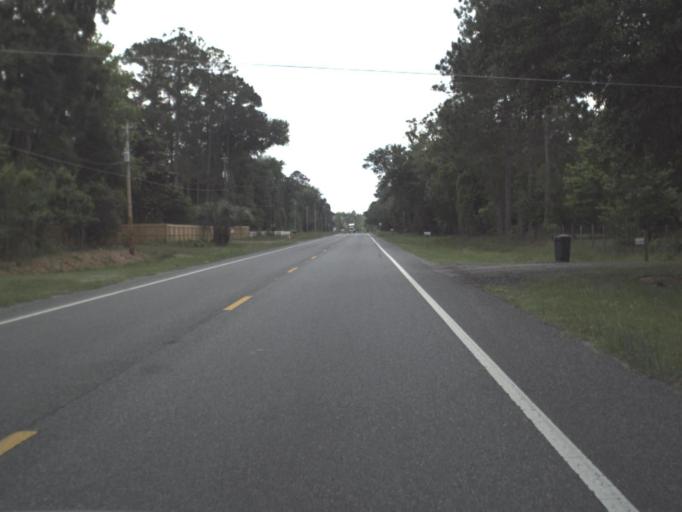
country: US
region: Florida
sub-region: Columbia County
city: Five Points
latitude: 30.2498
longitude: -82.6382
